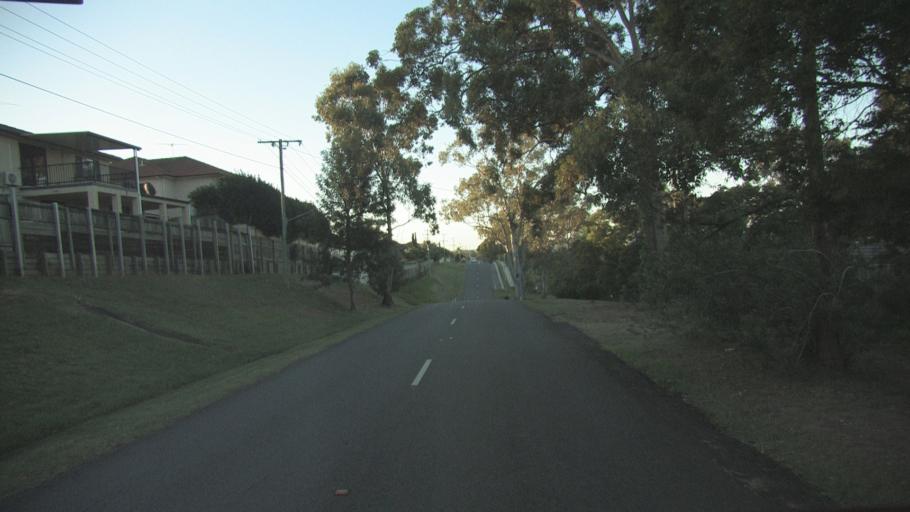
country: AU
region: Queensland
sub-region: Logan
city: Rochedale South
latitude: -27.6039
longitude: 153.1039
